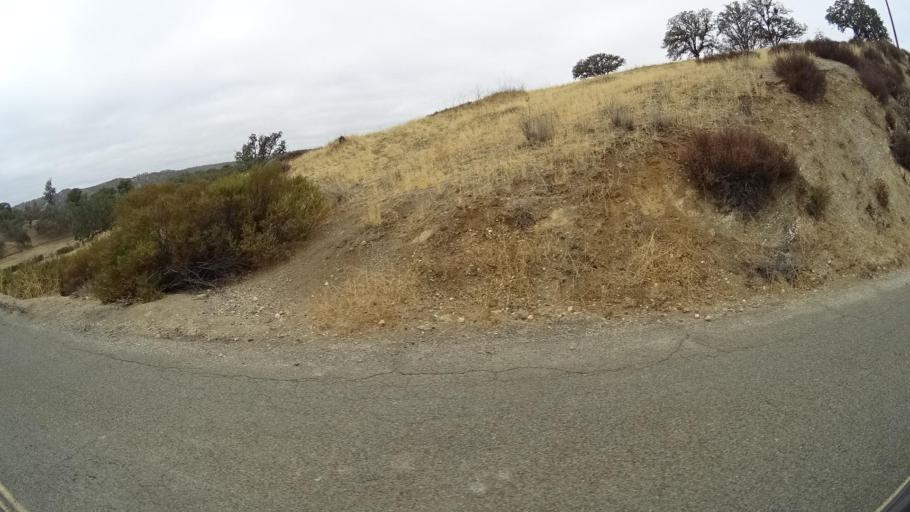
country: US
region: California
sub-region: San Luis Obispo County
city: Lake Nacimiento
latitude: 35.8623
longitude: -120.9675
